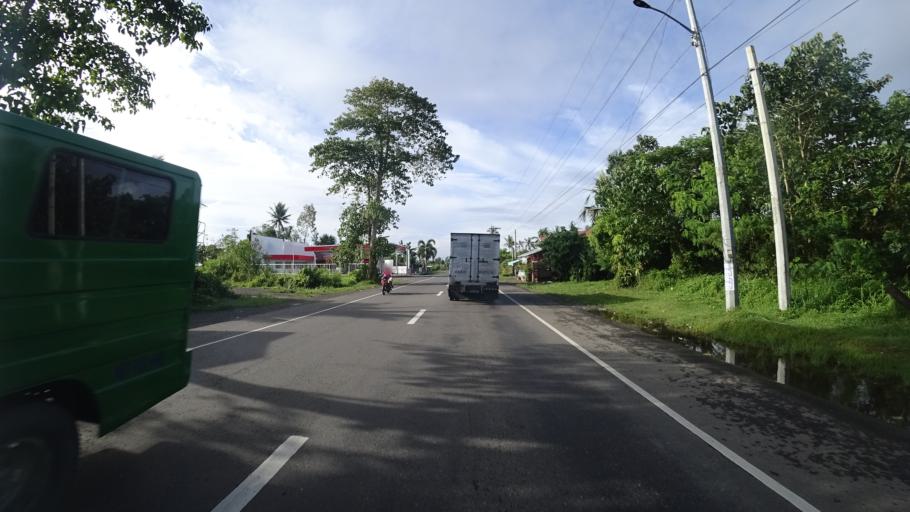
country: PH
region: Eastern Visayas
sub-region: Province of Leyte
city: Tanauan
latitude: 11.1165
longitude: 125.0178
